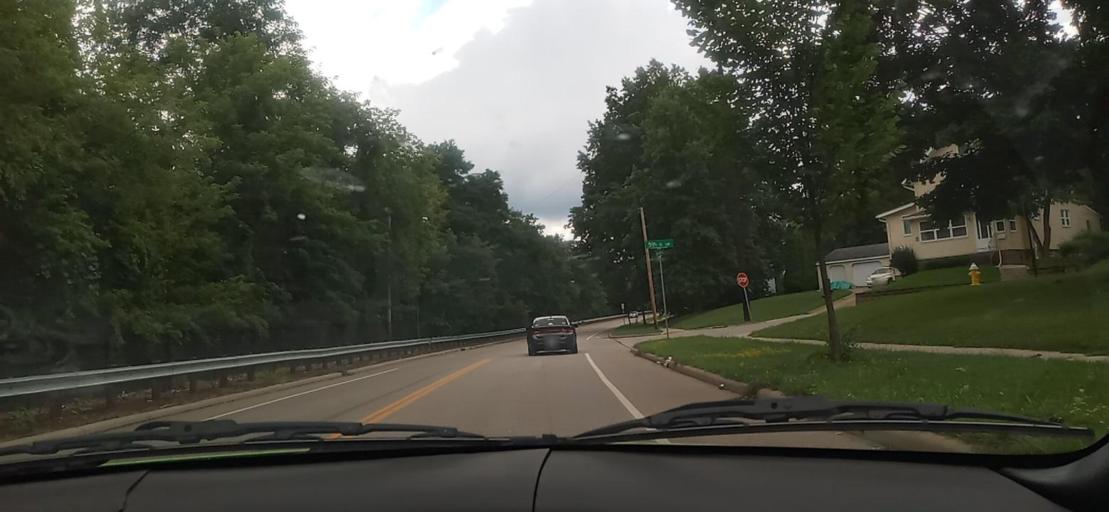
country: US
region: Ohio
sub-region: Summit County
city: Portage Lakes
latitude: 41.0414
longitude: -81.5488
